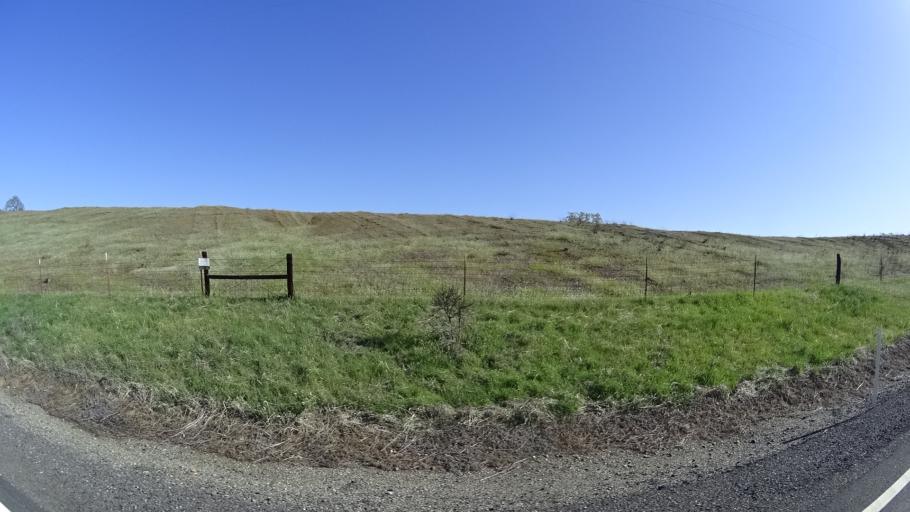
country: US
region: California
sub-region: Glenn County
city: Orland
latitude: 39.6578
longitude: -122.5637
